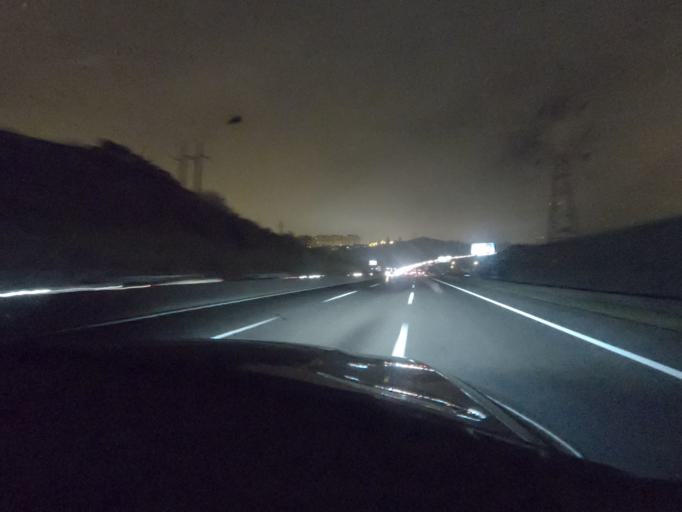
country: PT
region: Lisbon
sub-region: Vila Franca de Xira
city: Vialonga
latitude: 38.8748
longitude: -9.0668
